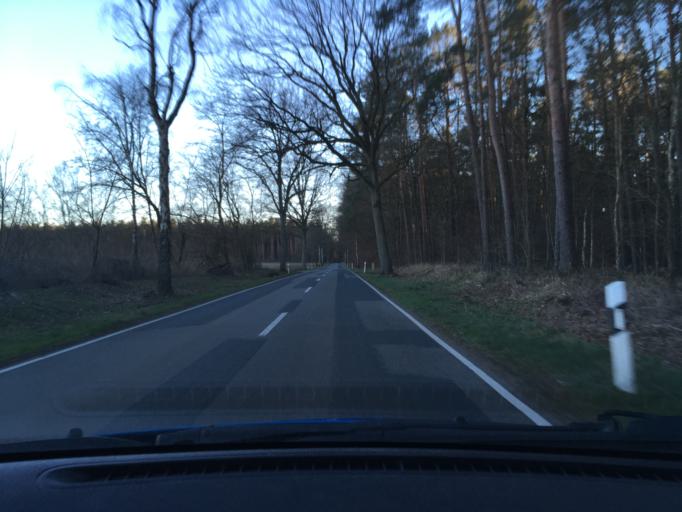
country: DE
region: Lower Saxony
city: Dahlem
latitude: 53.2444
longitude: 10.7488
